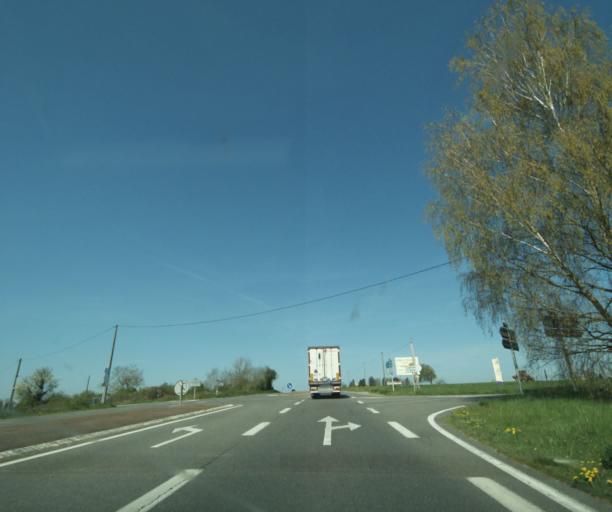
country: FR
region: Bourgogne
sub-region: Departement de la Nievre
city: Chantenay-Saint-Imbert
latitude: 46.7356
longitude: 3.1655
